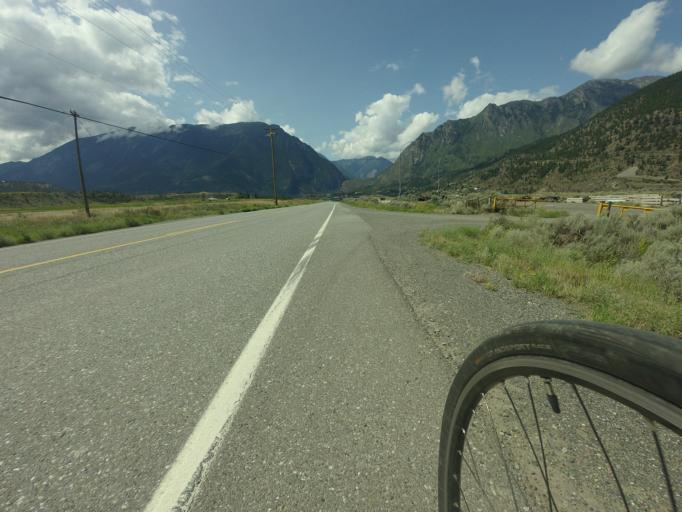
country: CA
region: British Columbia
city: Lillooet
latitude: 50.7044
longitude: -121.9104
